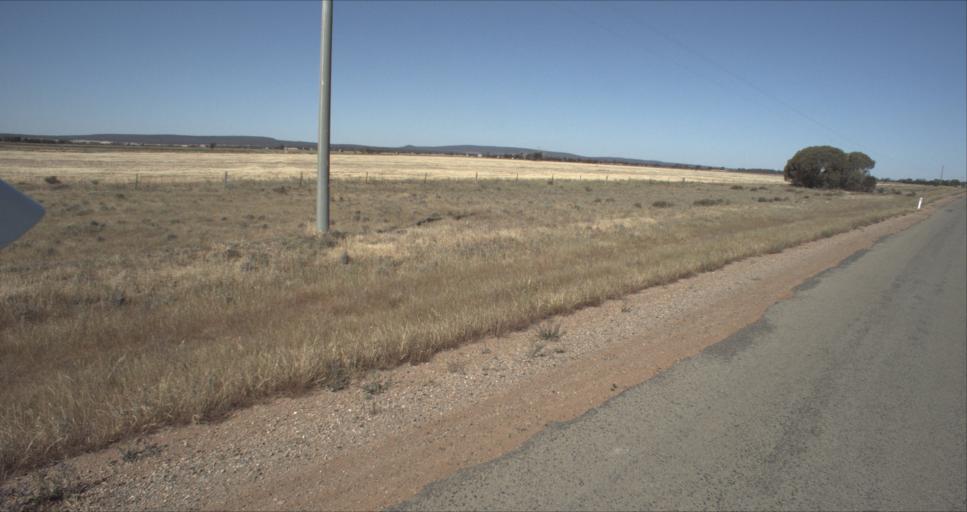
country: AU
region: New South Wales
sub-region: Leeton
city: Leeton
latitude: -34.4879
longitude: 146.3795
